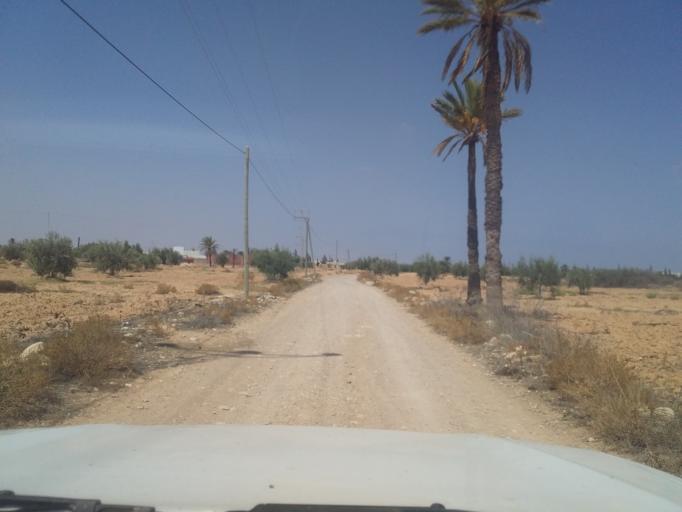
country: TN
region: Qabis
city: Matmata
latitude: 33.5965
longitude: 10.2824
